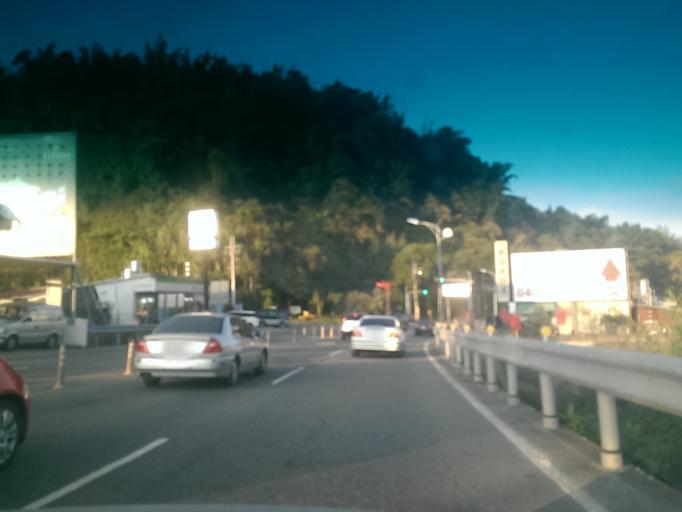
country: TW
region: Taiwan
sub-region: Nantou
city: Puli
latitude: 23.9436
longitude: 120.9310
